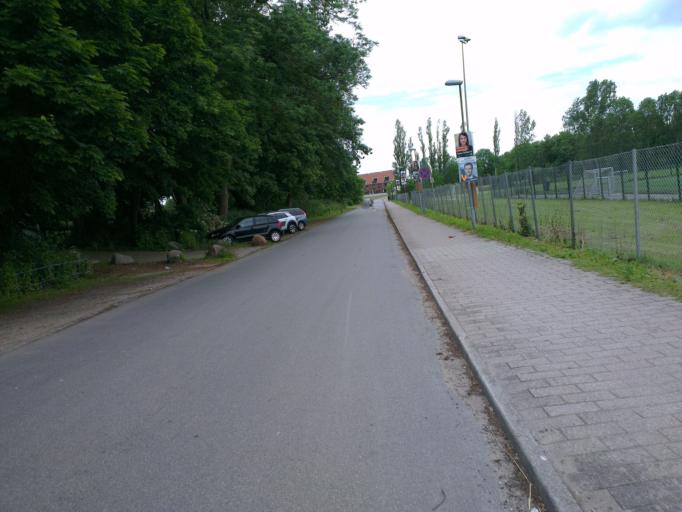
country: DK
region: Capital Region
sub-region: Frederikssund Kommune
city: Frederikssund
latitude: 55.8324
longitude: 12.0593
